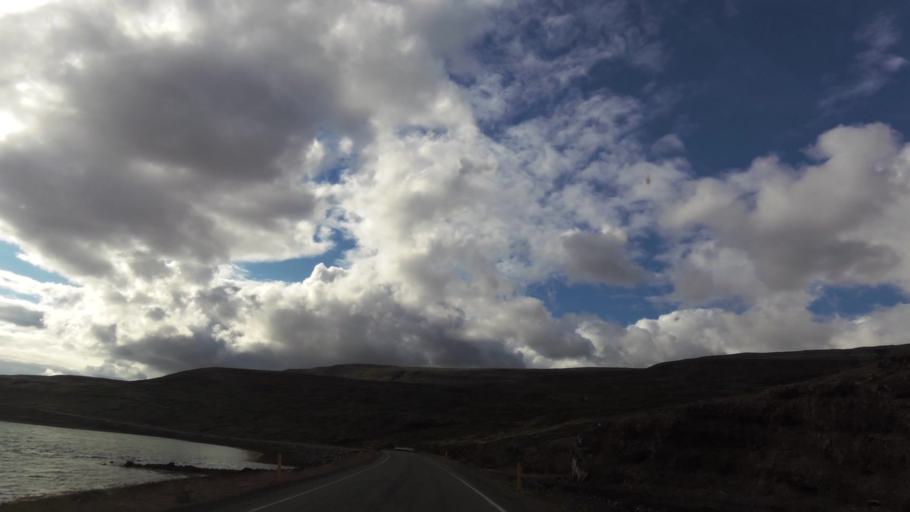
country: IS
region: West
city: Olafsvik
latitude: 65.5367
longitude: -23.7877
